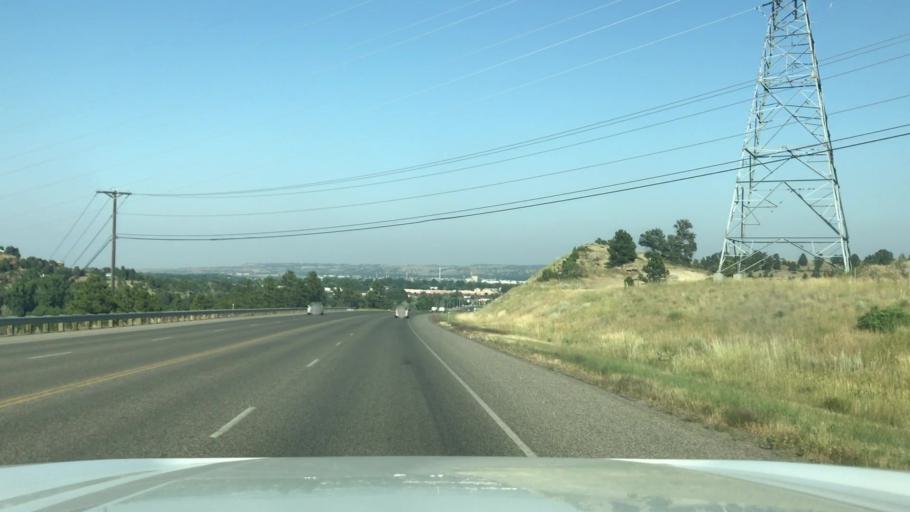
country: US
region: Montana
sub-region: Yellowstone County
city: Billings
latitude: 45.8011
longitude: -108.4940
